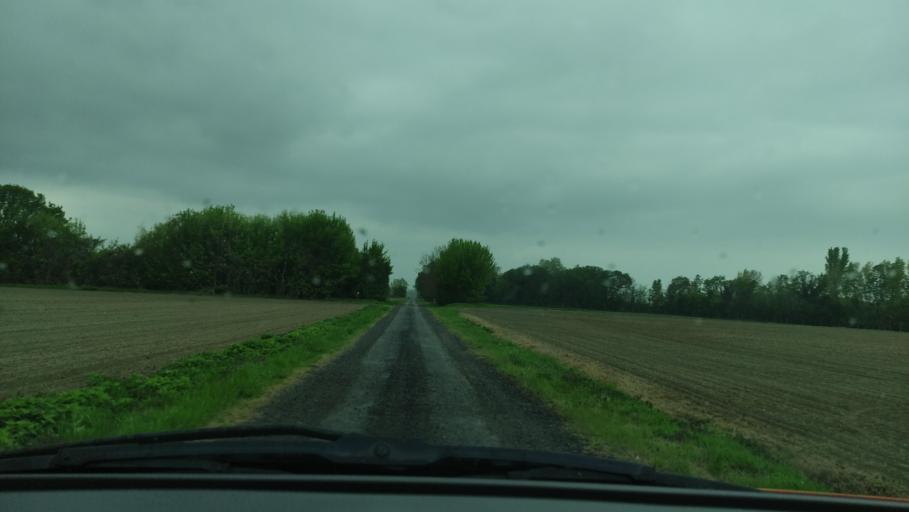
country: HR
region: Osjecko-Baranjska
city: Batina
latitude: 45.8972
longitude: 18.7851
